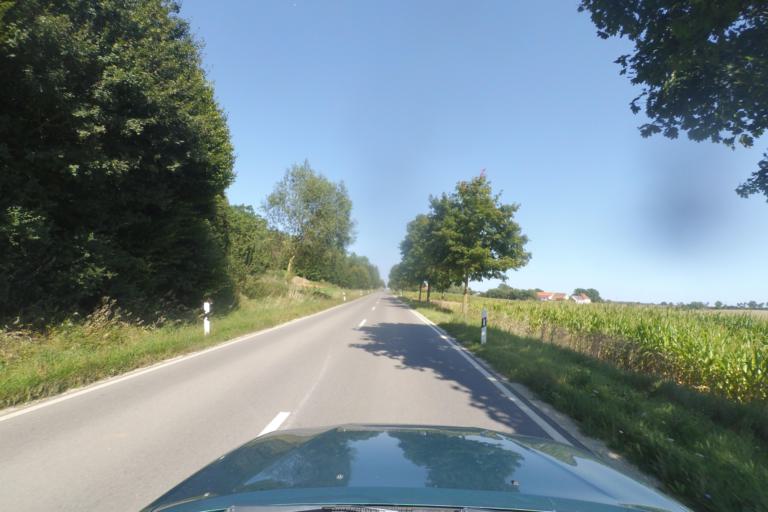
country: DE
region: Bavaria
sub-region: Swabia
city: Harburg
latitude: 48.7871
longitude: 10.7063
